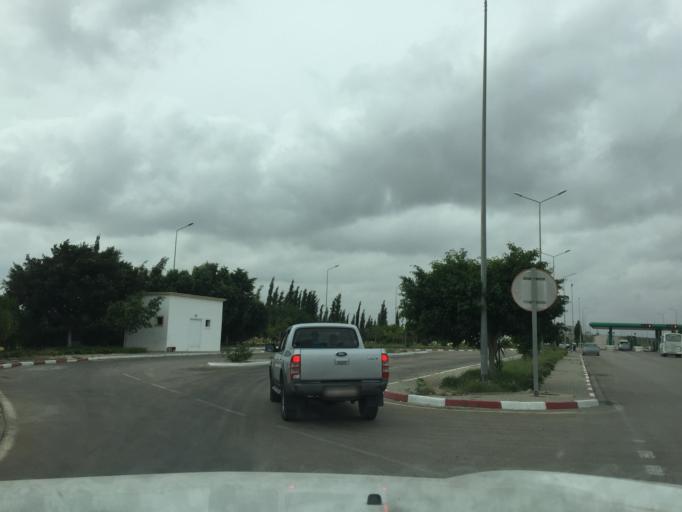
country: TN
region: Susah
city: Masakin
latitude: 35.6459
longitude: 10.5843
